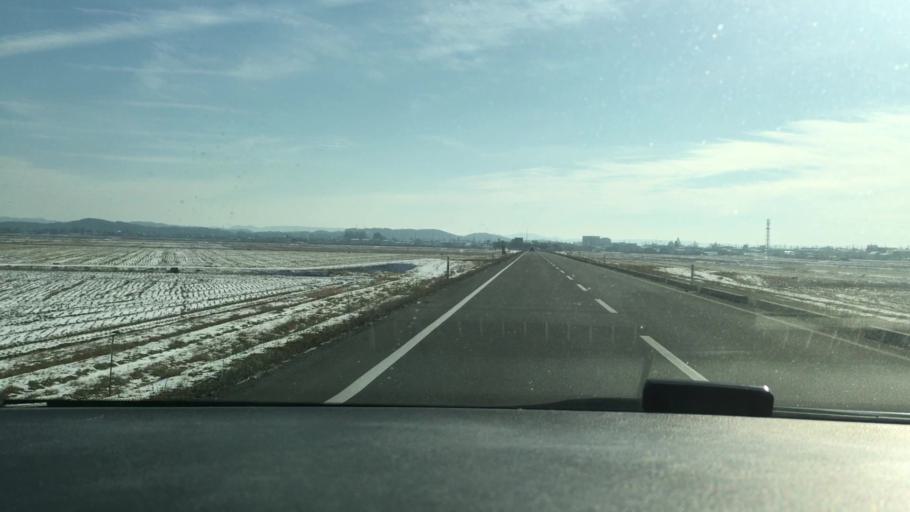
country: JP
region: Iwate
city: Ichinoseki
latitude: 38.7820
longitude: 141.1236
